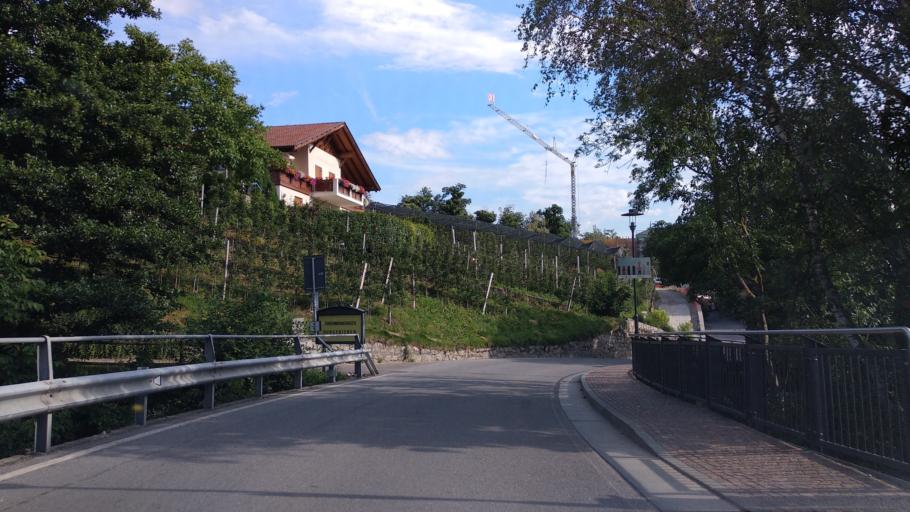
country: IT
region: Trentino-Alto Adige
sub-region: Bolzano
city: Scena
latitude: 46.6926
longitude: 11.1902
